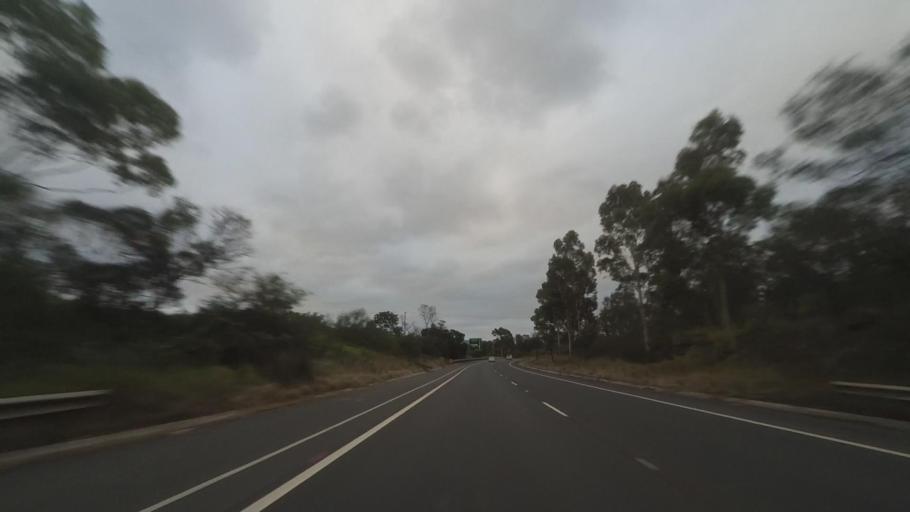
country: AU
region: New South Wales
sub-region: Shellharbour
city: Albion Park Rail
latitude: -34.5329
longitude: 150.7860
